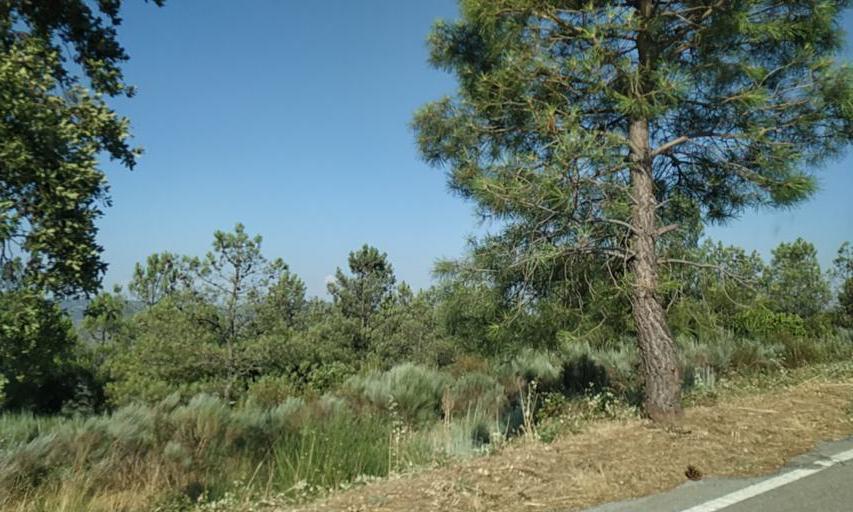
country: PT
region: Viseu
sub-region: Sao Joao da Pesqueira
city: Sao Joao da Pesqueira
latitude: 41.1693
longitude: -7.4368
